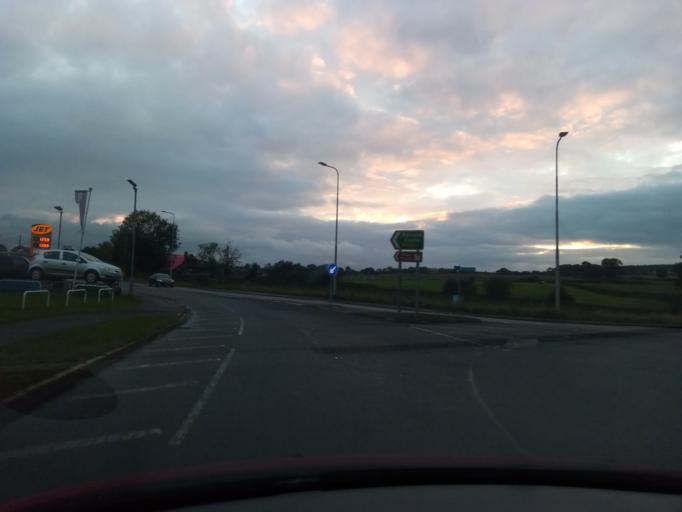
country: GB
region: England
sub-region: County Durham
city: High Etherley
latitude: 54.6263
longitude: -1.7260
